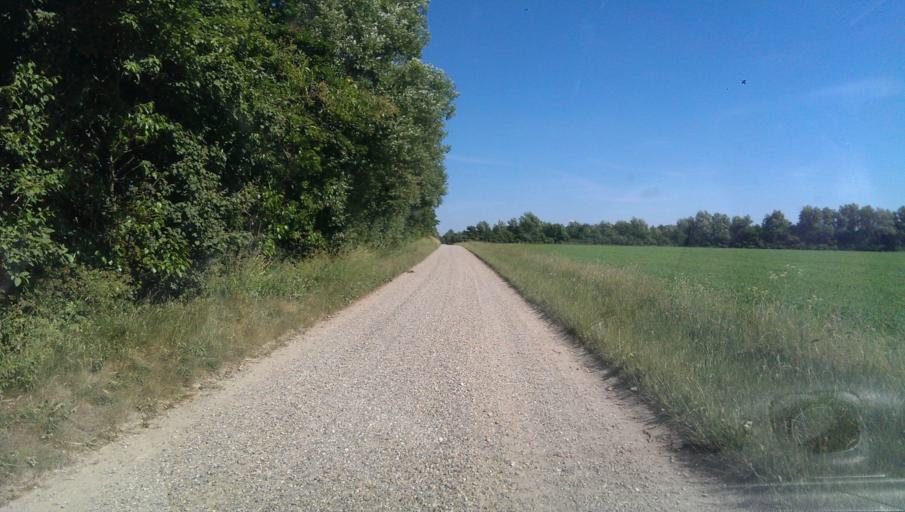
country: DK
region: South Denmark
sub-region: Fano Kommune
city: Nordby
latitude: 55.5298
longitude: 8.3848
